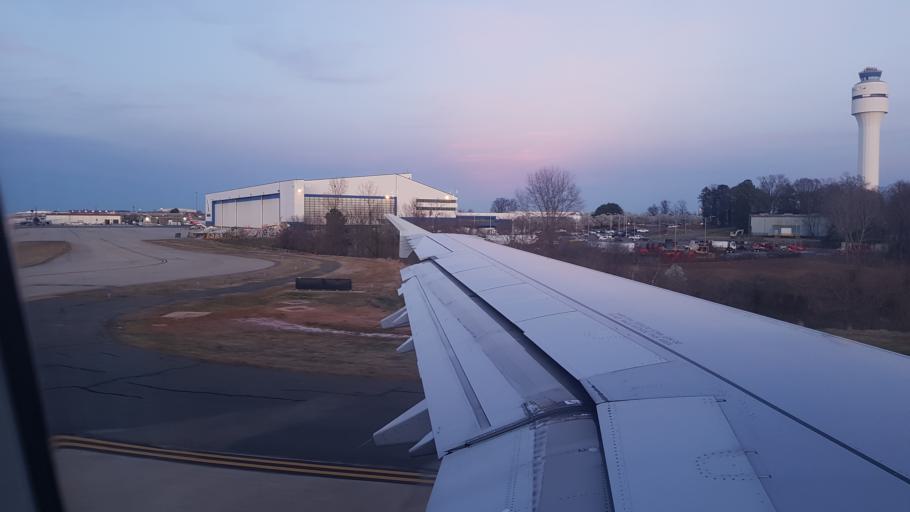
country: US
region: North Carolina
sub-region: Gaston County
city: Belmont
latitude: 35.2055
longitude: -80.9491
